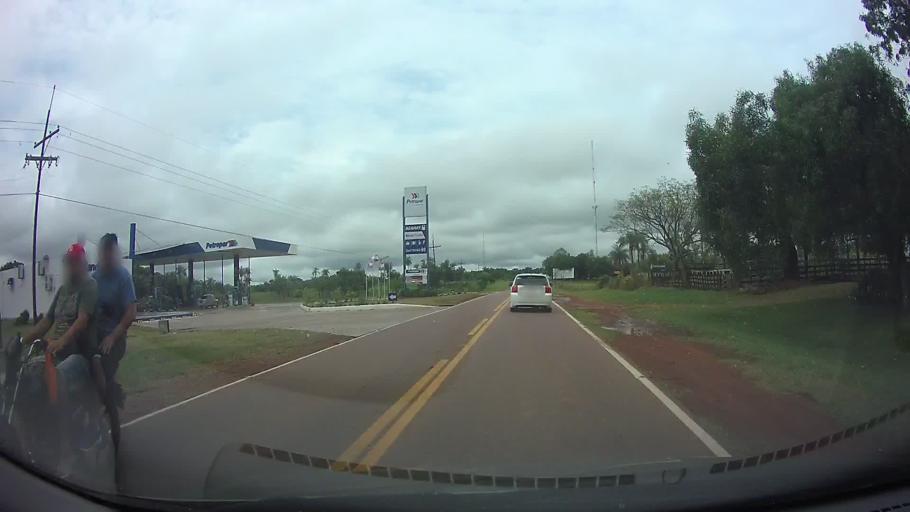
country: PY
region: Paraguari
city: Acahay
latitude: -25.8988
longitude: -57.1173
